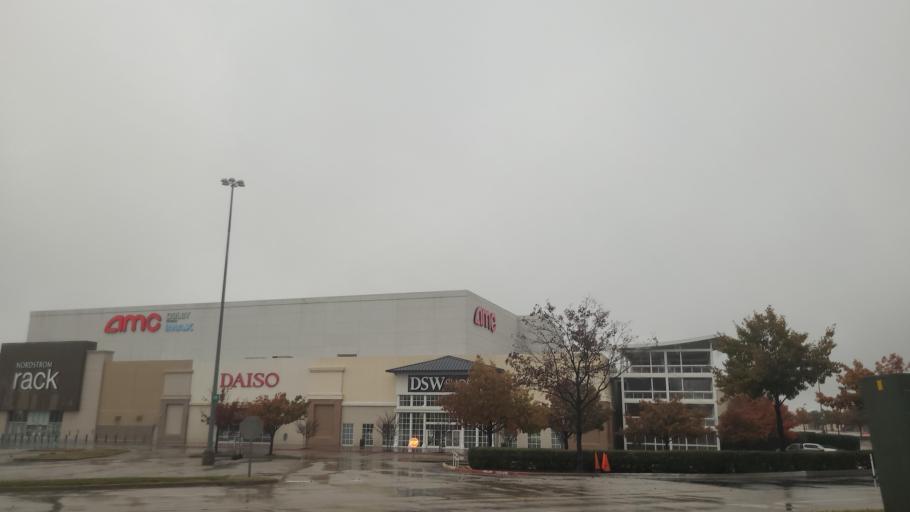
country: US
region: Texas
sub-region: Tarrant County
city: Dalworthington Gardens
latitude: 32.6775
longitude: -97.1273
